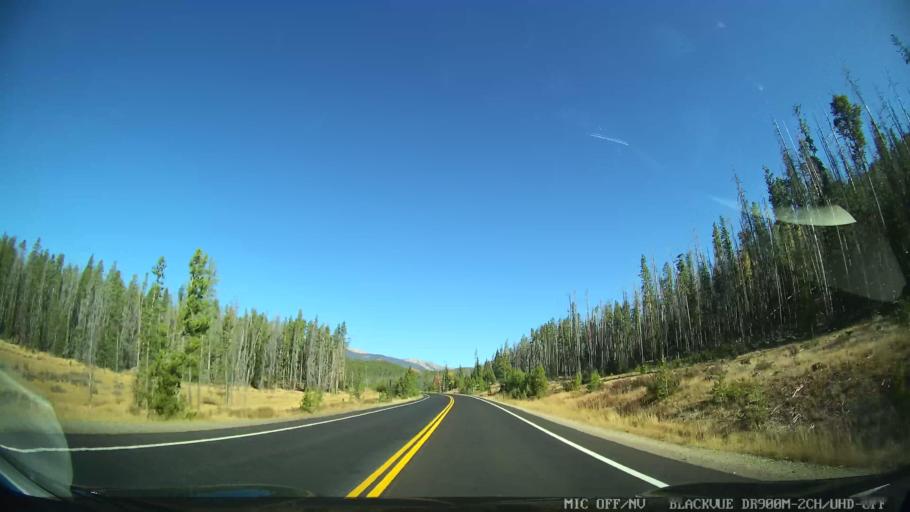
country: US
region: Colorado
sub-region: Grand County
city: Granby
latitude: 40.3134
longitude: -105.8429
